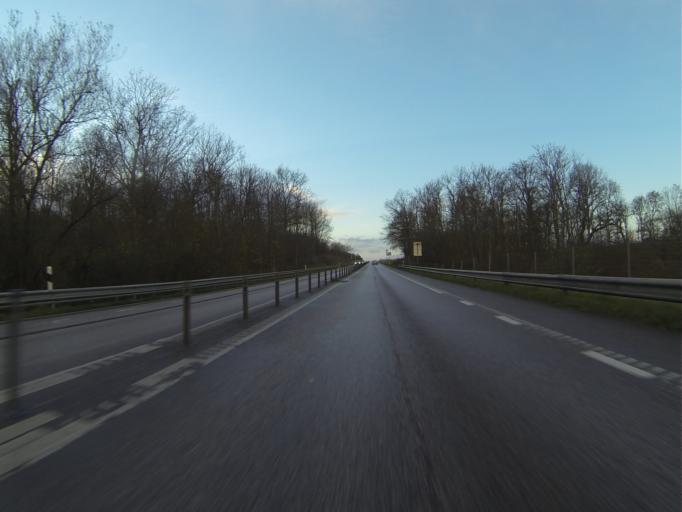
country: SE
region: Skane
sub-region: Trelleborgs Kommun
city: Anderslov
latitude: 55.5106
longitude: 13.3152
